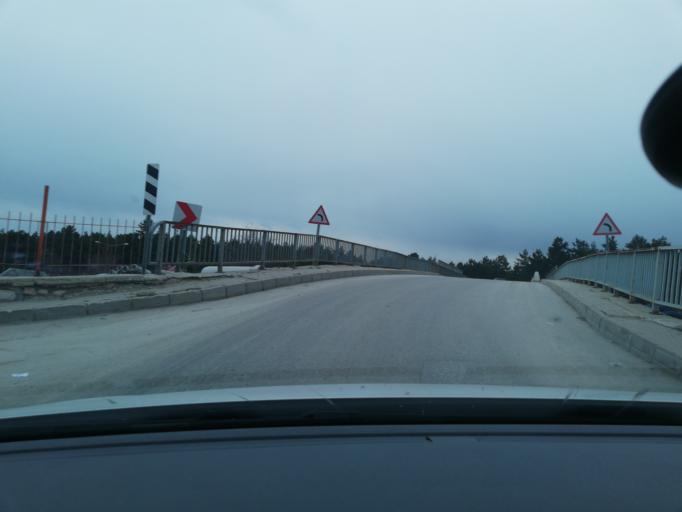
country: TR
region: Bolu
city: Gerede
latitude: 40.7950
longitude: 32.2056
